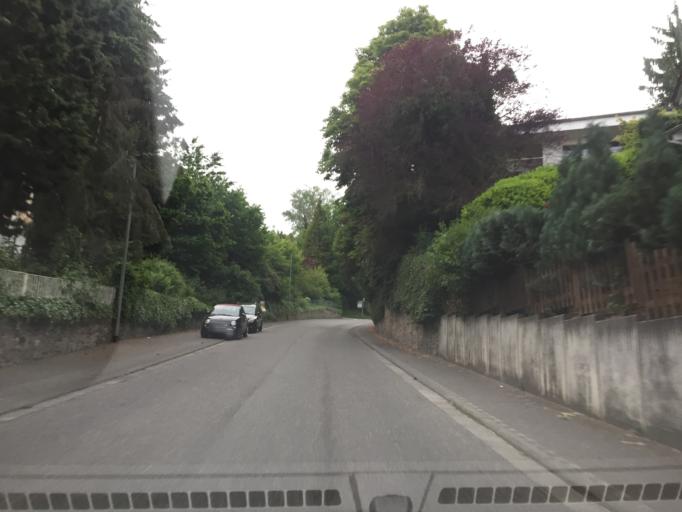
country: DE
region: Hesse
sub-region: Regierungsbezirk Giessen
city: Elz
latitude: 50.4490
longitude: 8.0423
